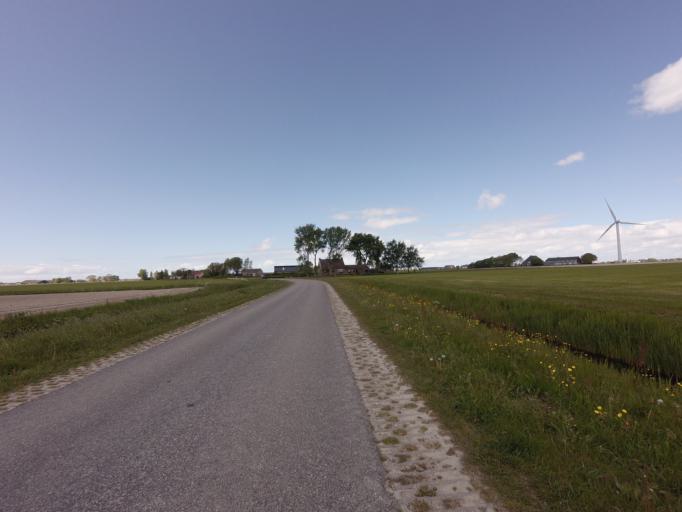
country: NL
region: Friesland
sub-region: Gemeente Harlingen
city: Harlingen
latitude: 53.1191
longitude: 5.4340
